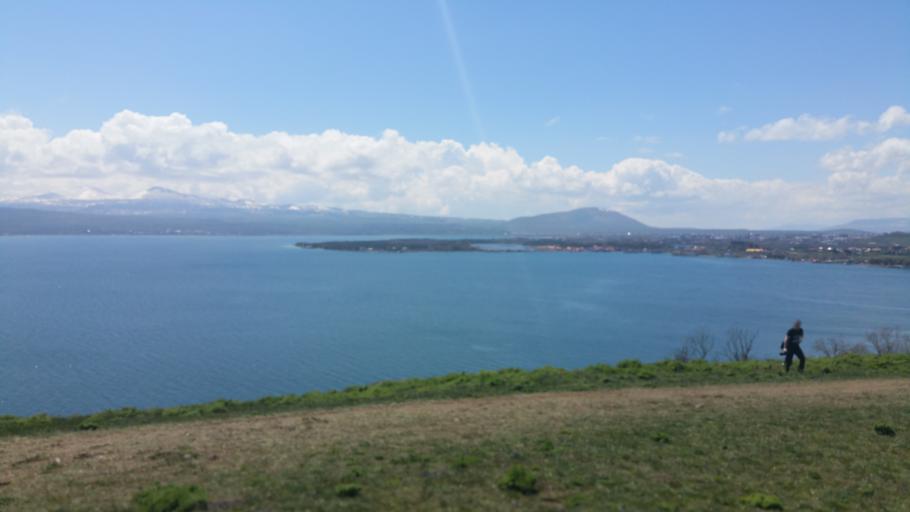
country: AM
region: Geghark'unik'i Marz
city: Sevan
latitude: 40.5639
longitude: 45.0129
